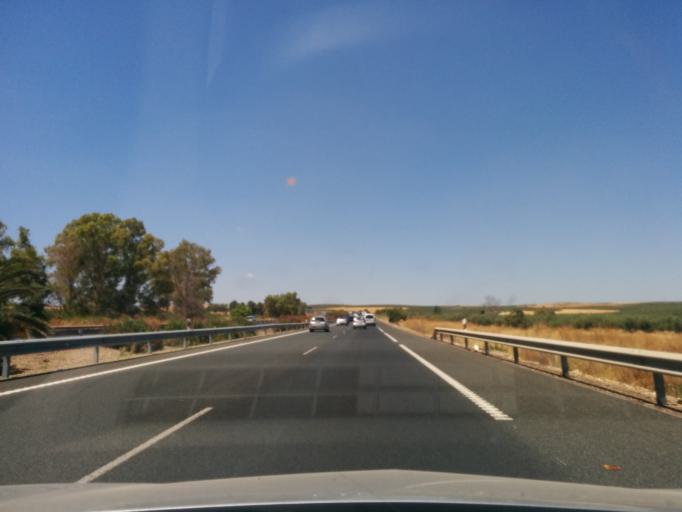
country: ES
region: Andalusia
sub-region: Provincia de Sevilla
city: Carrion de los Cespedes
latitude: 37.3612
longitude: -6.2849
